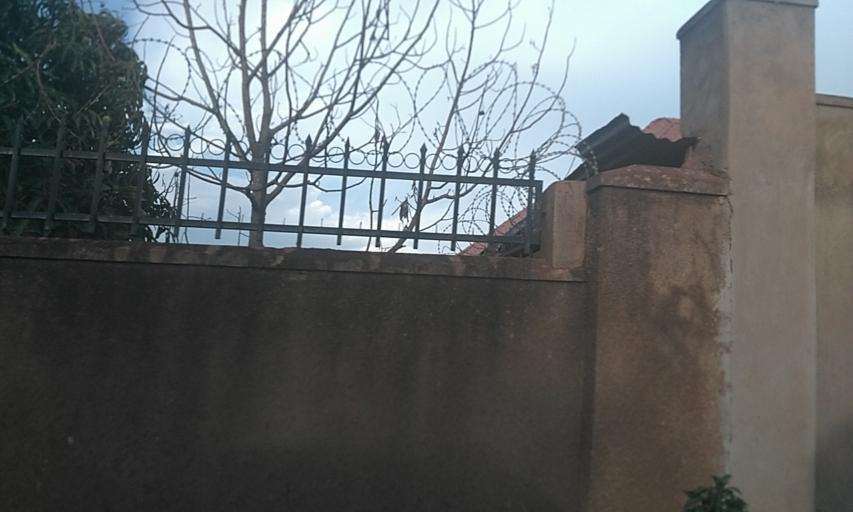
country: UG
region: Central Region
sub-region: Wakiso District
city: Kajansi
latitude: 0.2613
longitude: 32.5310
